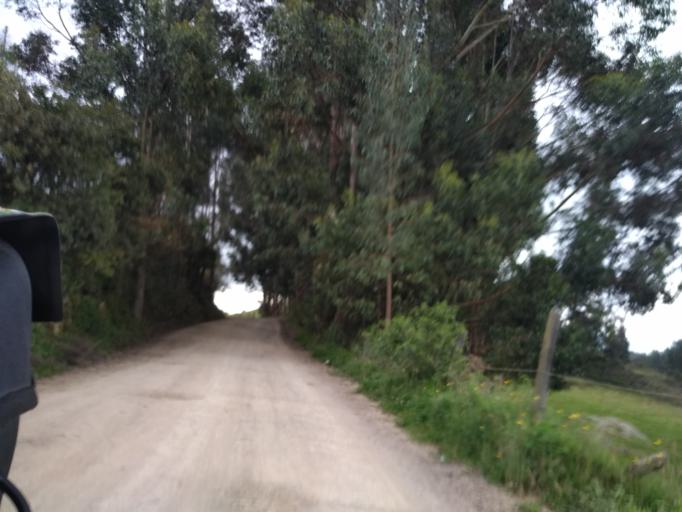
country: CO
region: Boyaca
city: Sotaquira
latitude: 5.7589
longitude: -73.2834
